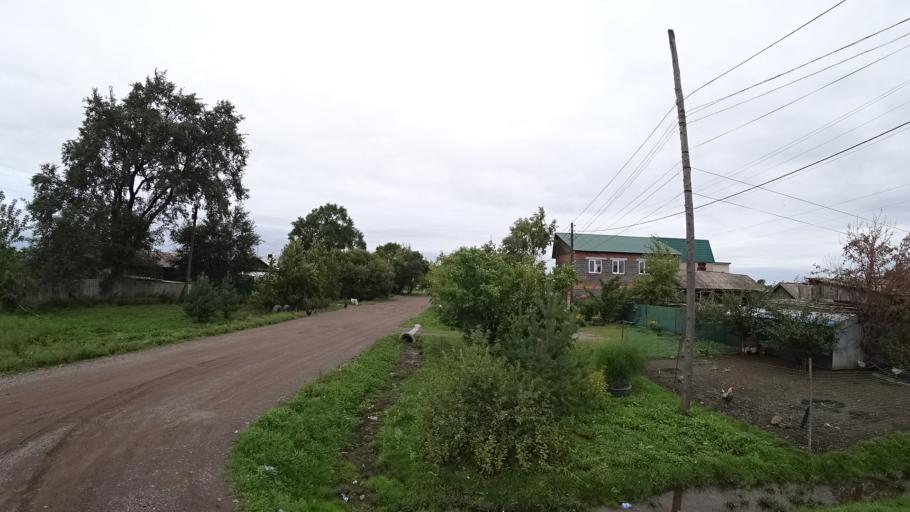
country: RU
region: Primorskiy
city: Chernigovka
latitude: 44.3351
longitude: 132.5667
